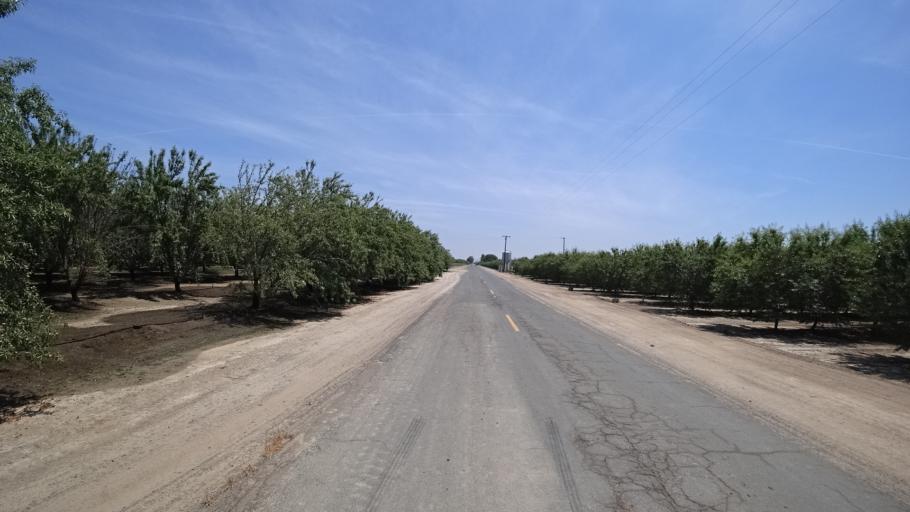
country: US
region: California
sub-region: Fresno County
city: Riverdale
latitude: 36.3875
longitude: -119.8838
